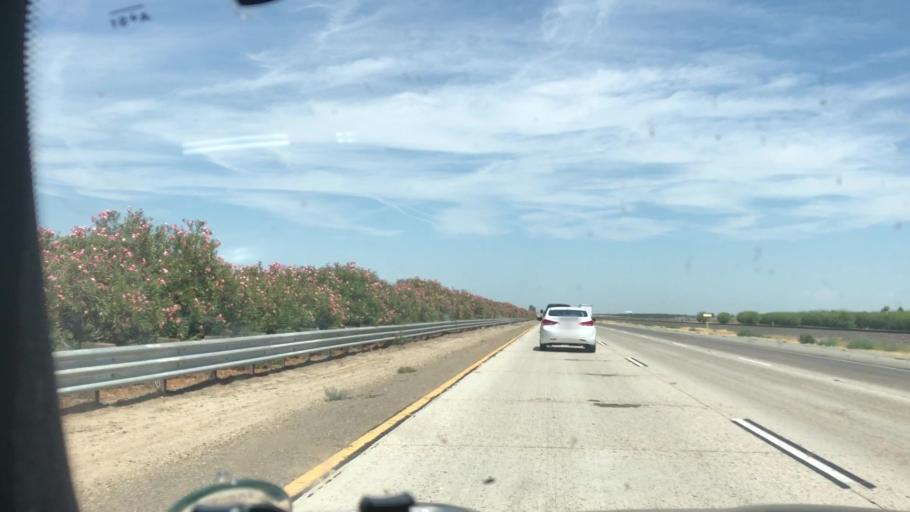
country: US
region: California
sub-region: Kern County
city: McFarland
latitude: 35.6274
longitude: -119.2152
